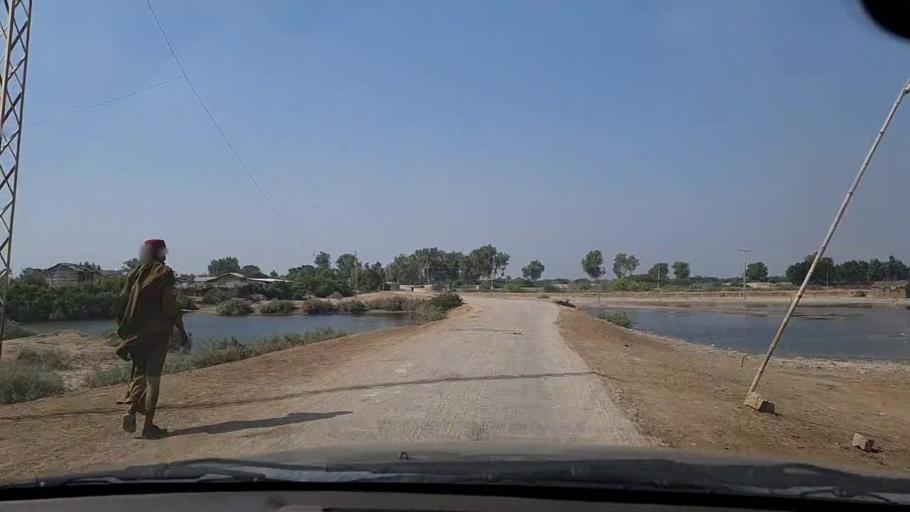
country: PK
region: Sindh
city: Chuhar Jamali
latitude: 24.4229
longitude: 67.8205
